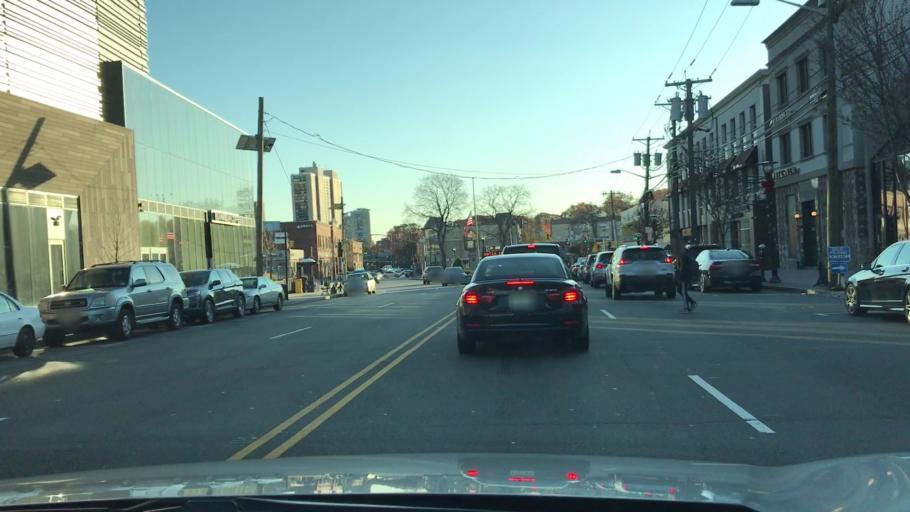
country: US
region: New Jersey
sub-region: Bergen County
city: Fort Lee
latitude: 40.8523
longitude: -73.9694
